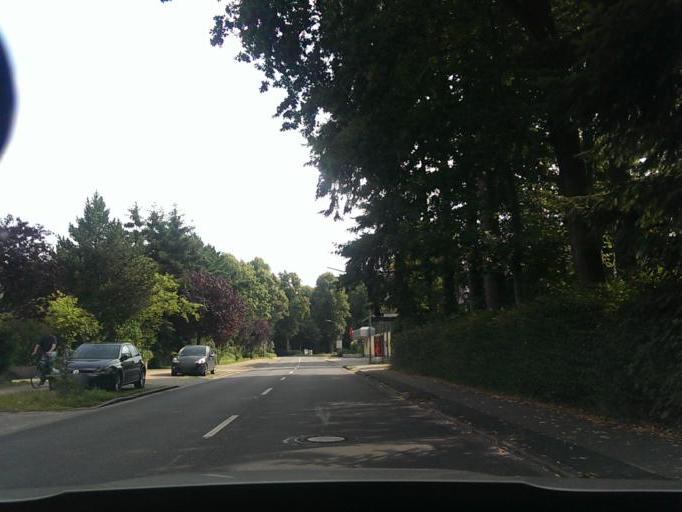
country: DE
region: Hamburg
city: Poppenbuettel
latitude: 53.6616
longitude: 10.0866
